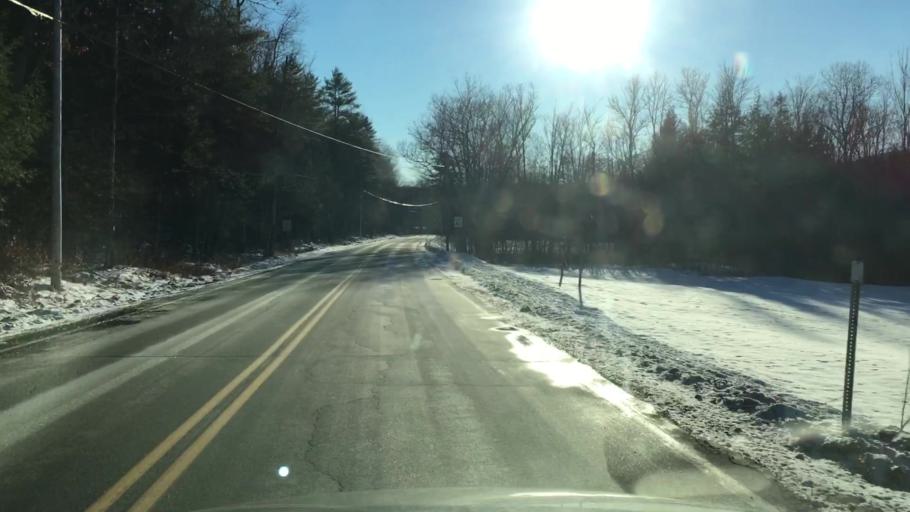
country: US
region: New Hampshire
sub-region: Grafton County
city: Woodsville
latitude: 44.2019
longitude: -72.0555
